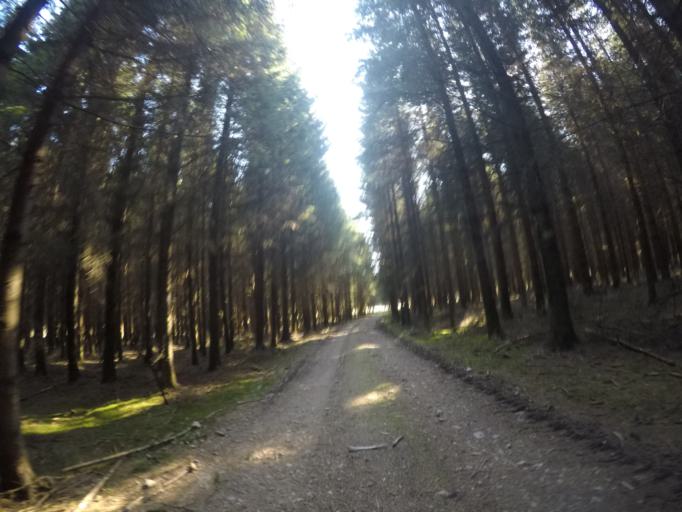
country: BE
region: Wallonia
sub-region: Province du Luxembourg
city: Leglise
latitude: 49.8006
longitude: 5.5878
